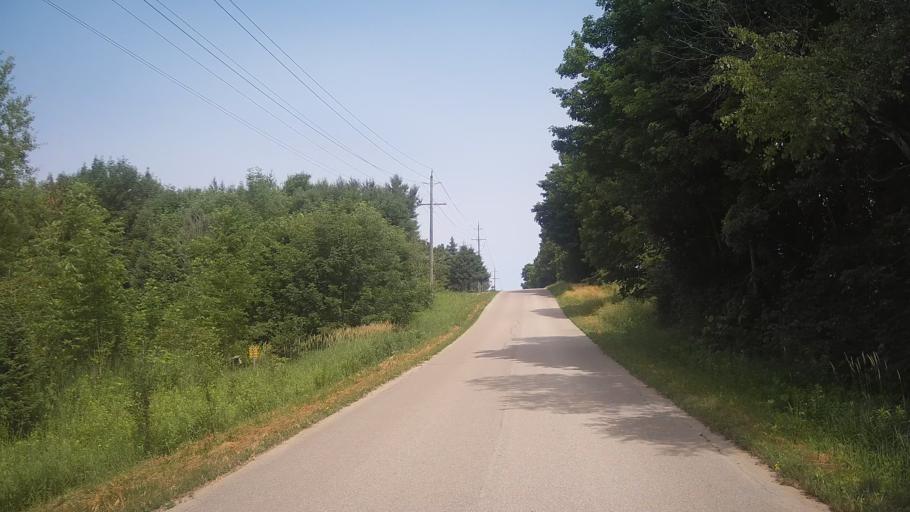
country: CA
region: Ontario
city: Barrie
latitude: 44.4523
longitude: -79.6275
